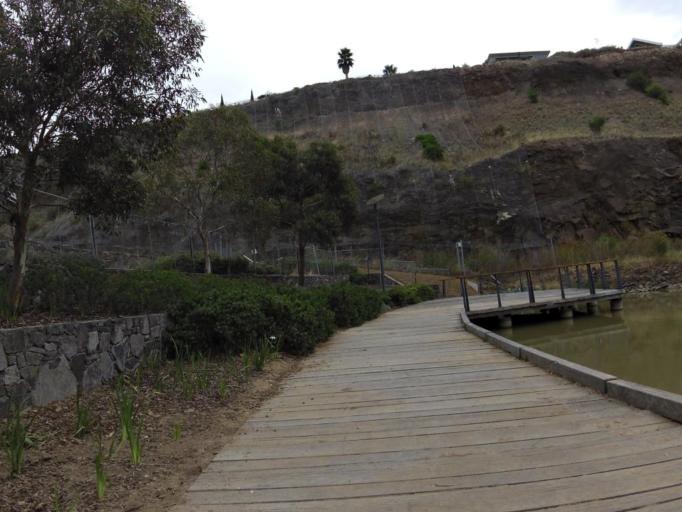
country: AU
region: Victoria
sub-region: Moonee Valley
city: Keilor East
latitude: -37.7403
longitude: 144.8748
